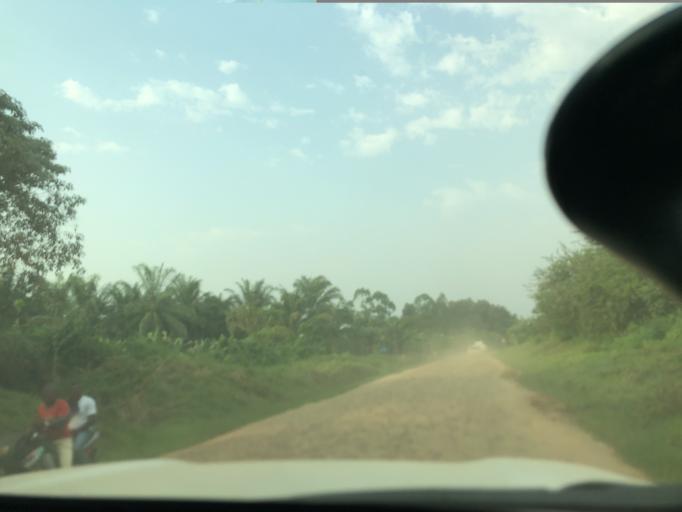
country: UG
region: Western Region
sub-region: Kasese District
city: Margherita
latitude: 0.3076
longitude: 29.6670
